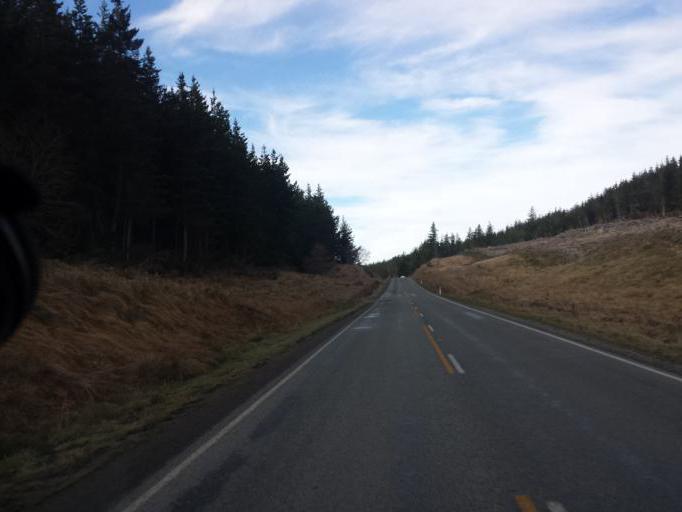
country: NZ
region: Canterbury
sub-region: Timaru District
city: Pleasant Point
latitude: -44.1223
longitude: 171.0705
